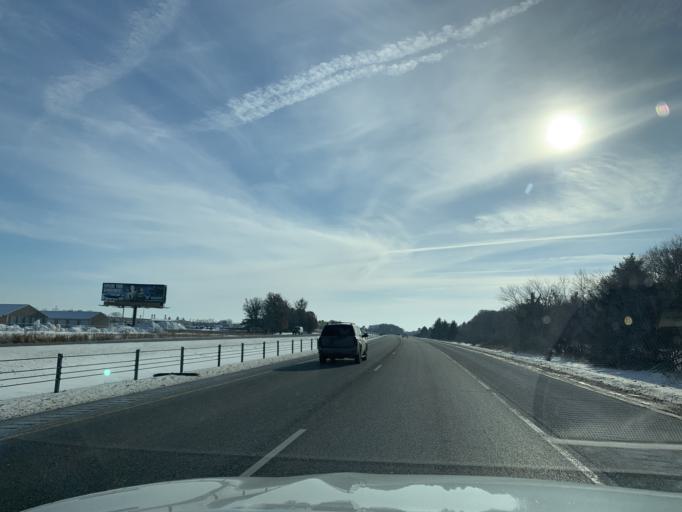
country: US
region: Minnesota
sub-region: Chisago County
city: Wyoming
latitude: 45.3302
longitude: -93.0048
